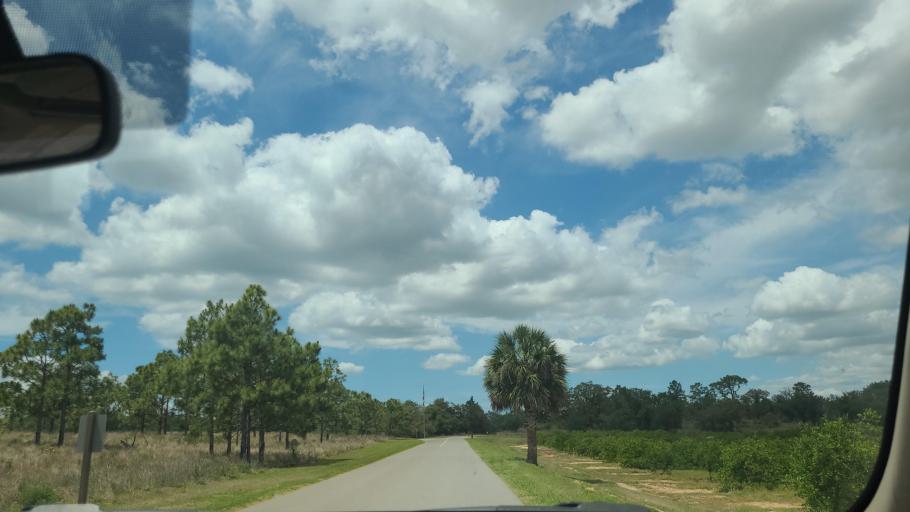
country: US
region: Florida
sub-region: Polk County
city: Lake Wales
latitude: 27.9343
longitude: -81.5707
